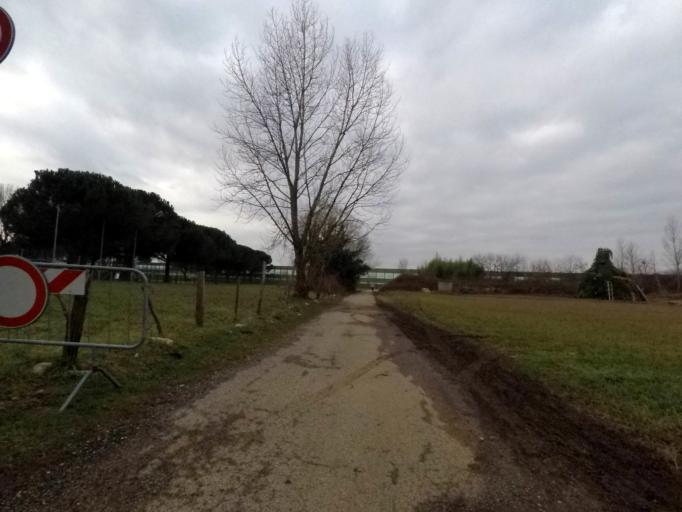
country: IT
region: Friuli Venezia Giulia
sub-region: Provincia di Udine
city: Colugna
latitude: 46.0938
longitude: 13.1984
